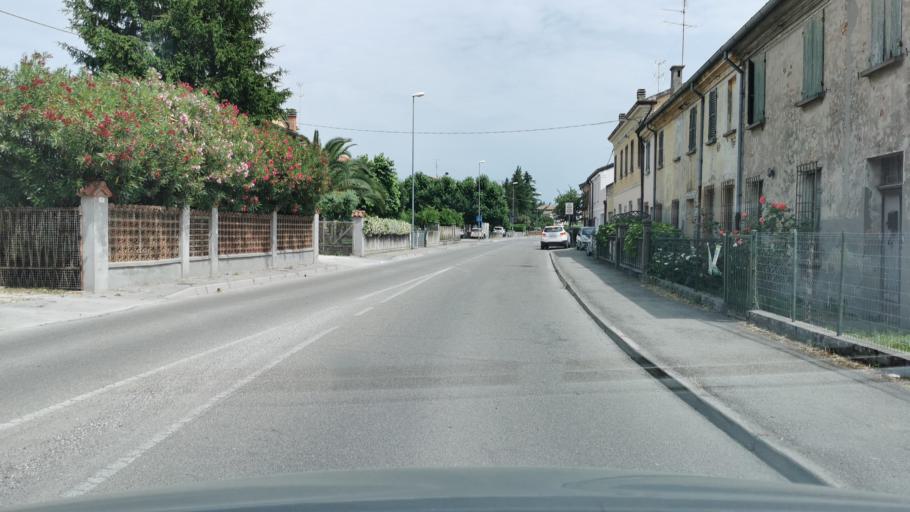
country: IT
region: Emilia-Romagna
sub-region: Provincia di Ravenna
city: Bagnacavallo
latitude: 44.4201
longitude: 11.9750
